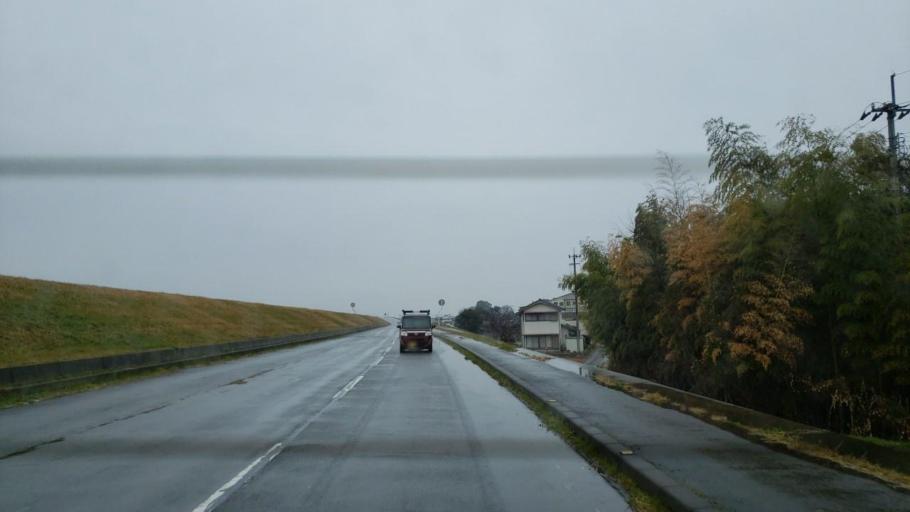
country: JP
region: Tokushima
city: Ishii
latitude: 34.1070
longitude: 134.4283
